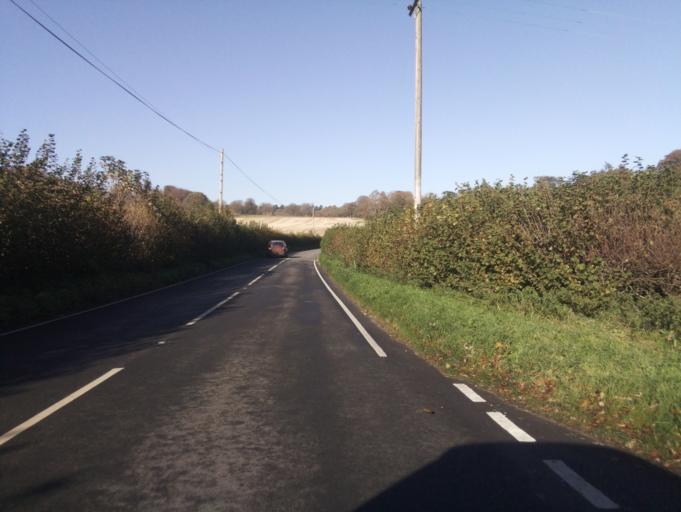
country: GB
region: England
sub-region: Dorset
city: Dorchester
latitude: 50.8278
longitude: -2.4809
